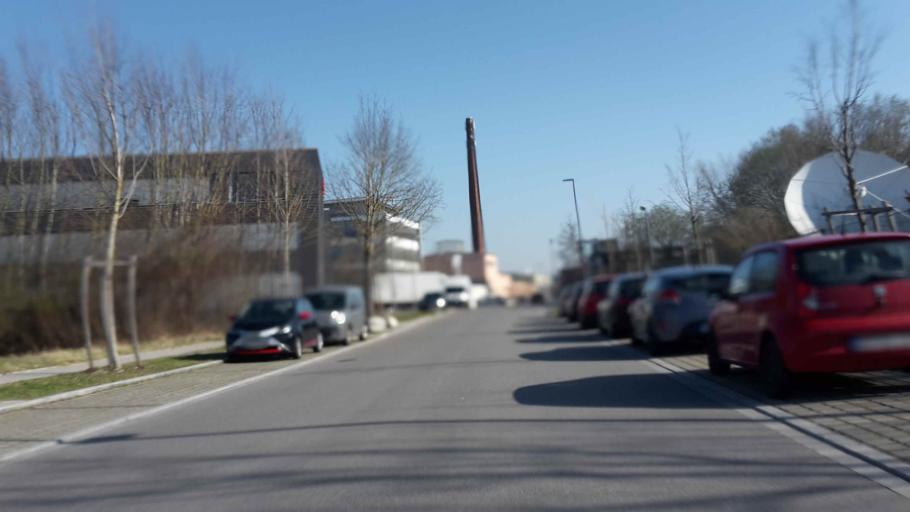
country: DE
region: Bavaria
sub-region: Upper Bavaria
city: Unterfoehring
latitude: 48.2072
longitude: 11.6579
